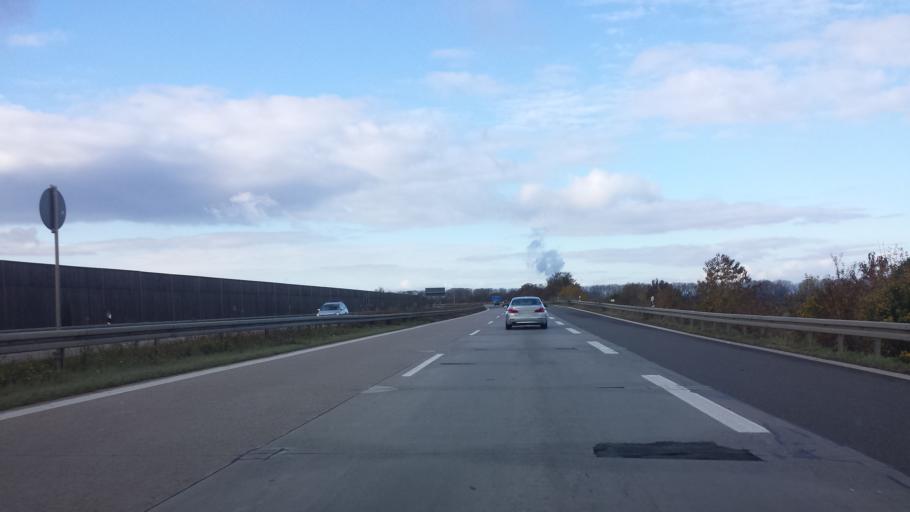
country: DE
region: Hesse
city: Lampertheim
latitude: 49.5532
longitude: 8.4379
